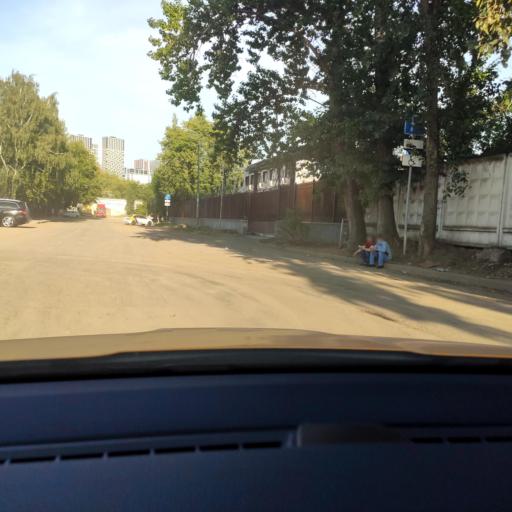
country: RU
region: Moskovskaya
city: Bogorodskoye
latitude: 55.8090
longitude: 37.7422
